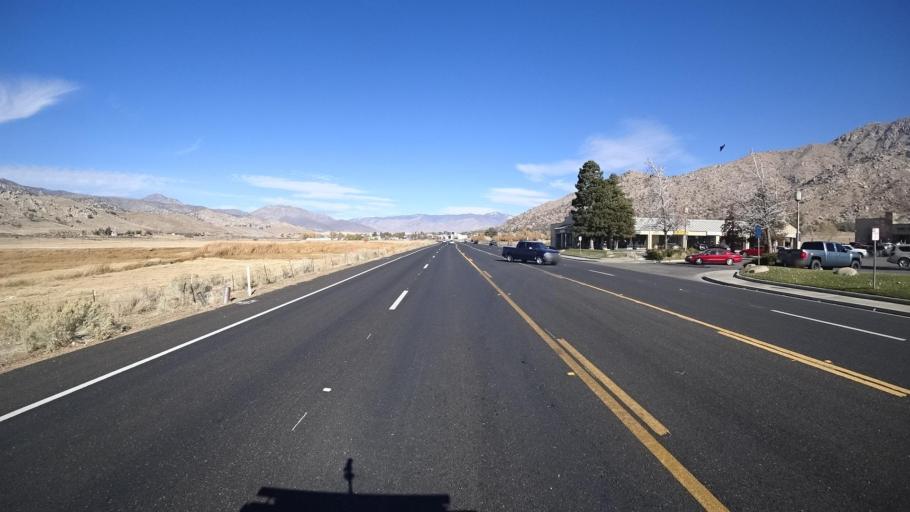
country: US
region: California
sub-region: Kern County
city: Lake Isabella
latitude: 35.6190
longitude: -118.4776
